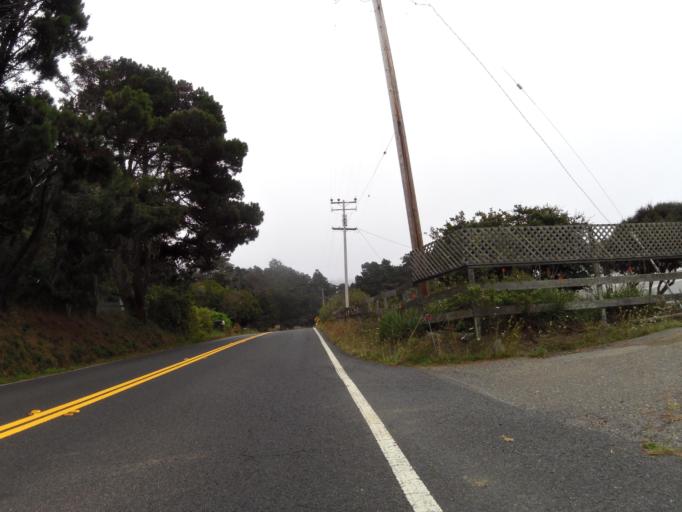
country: US
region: California
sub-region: Sonoma County
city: Monte Rio
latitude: 38.5289
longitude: -123.2653
